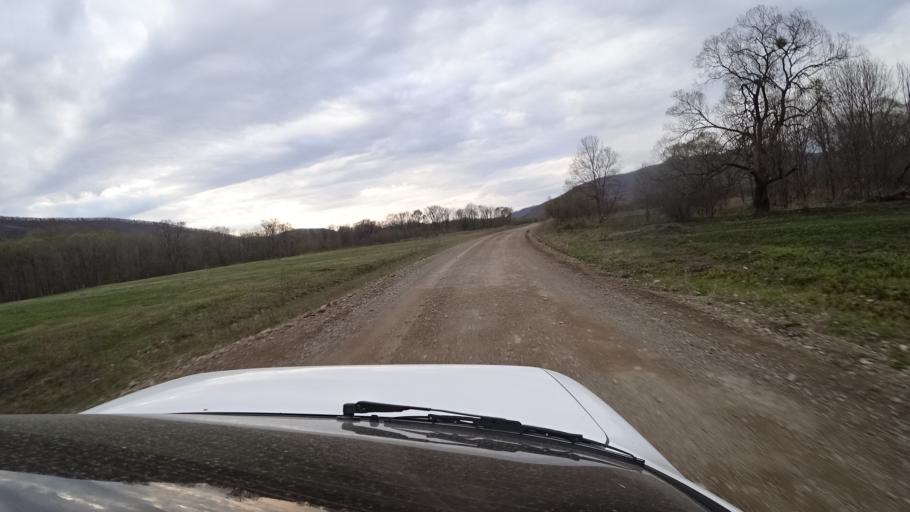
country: RU
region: Primorskiy
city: Novopokrovka
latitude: 45.1489
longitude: 134.3817
